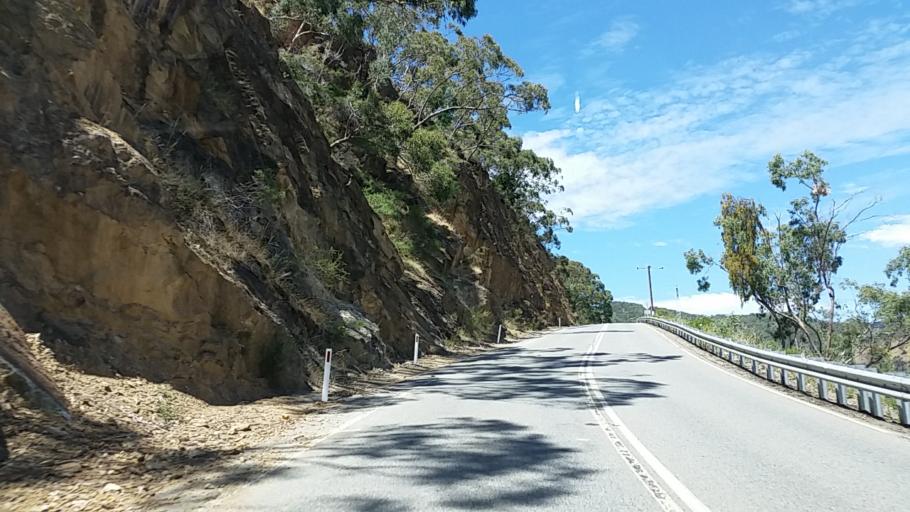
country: AU
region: South Australia
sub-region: Campbelltown
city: Athelstone
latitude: -34.8641
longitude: 138.7721
